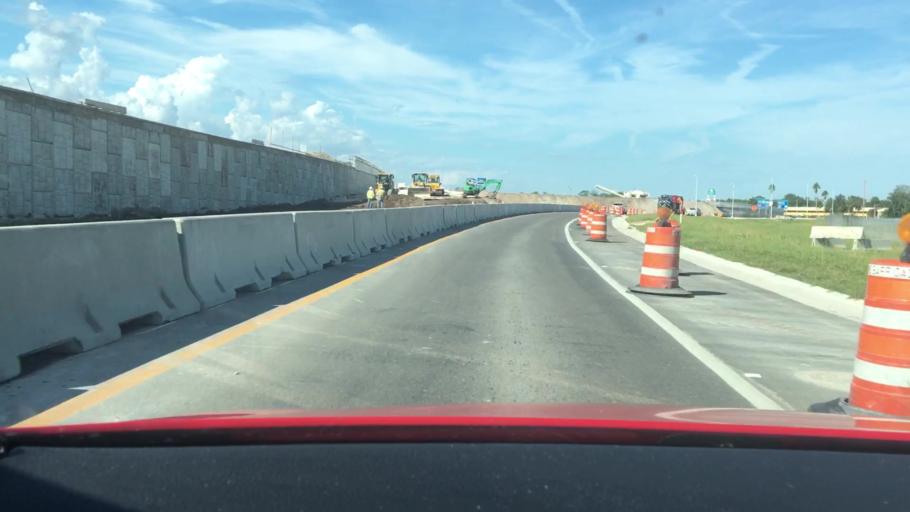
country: US
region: Florida
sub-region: Volusia County
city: Daytona Beach
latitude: 29.1691
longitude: -81.0828
